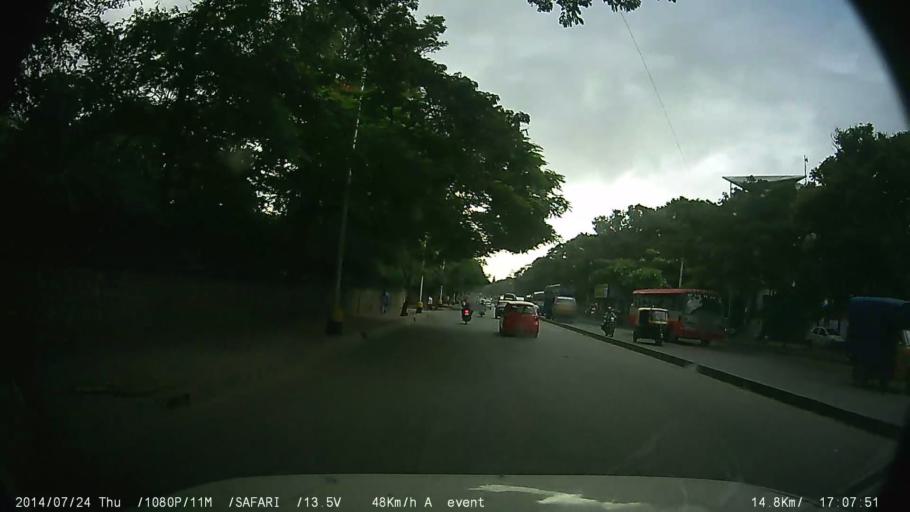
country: IN
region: Karnataka
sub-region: Bangalore Urban
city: Bangalore
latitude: 12.9265
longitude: 77.6234
